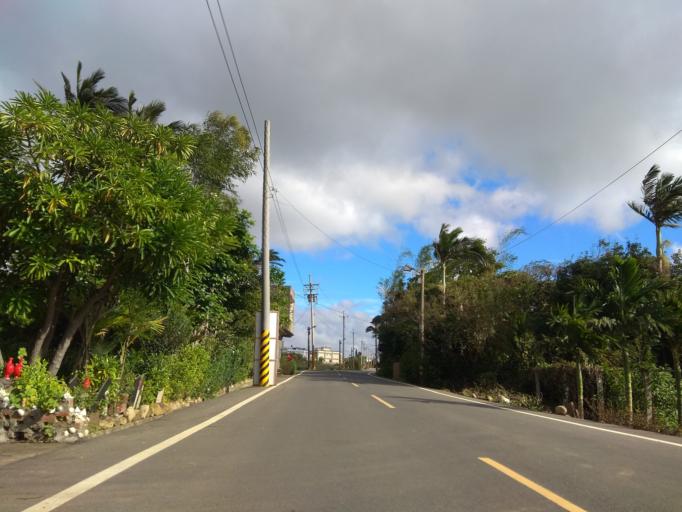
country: TW
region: Taiwan
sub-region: Hsinchu
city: Zhubei
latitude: 24.9686
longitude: 121.0904
